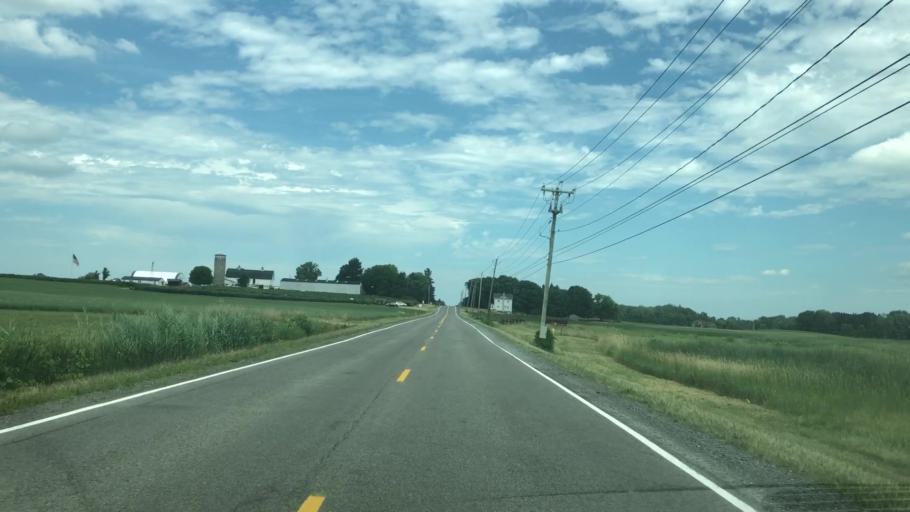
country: US
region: New York
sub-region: Monroe County
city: Webster
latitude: 43.1677
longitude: -77.4005
